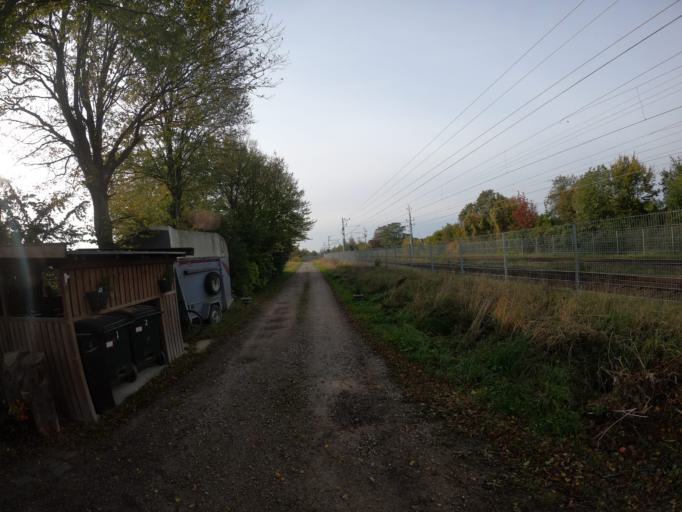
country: SE
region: Skane
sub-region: Lunds Kommun
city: Lund
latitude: 55.7550
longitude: 13.2038
